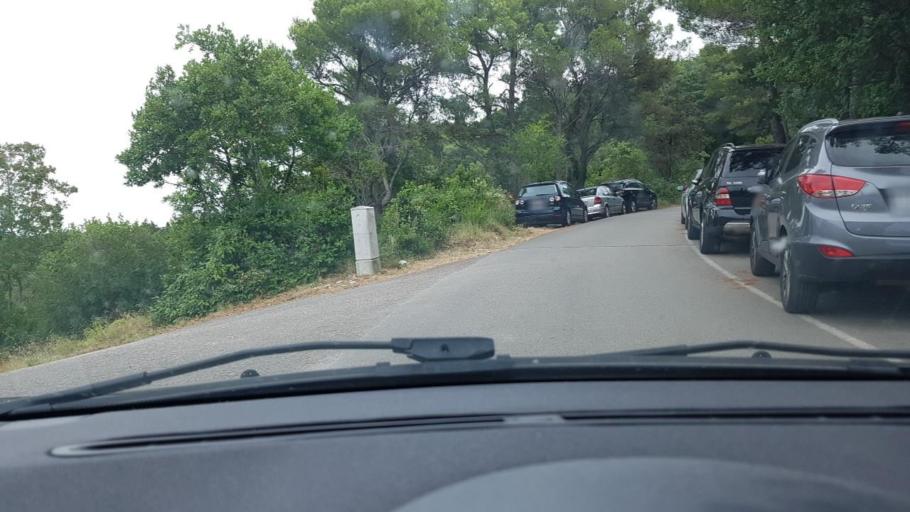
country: HR
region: Dubrovacko-Neretvanska
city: Korcula
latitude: 42.9611
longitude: 17.1295
